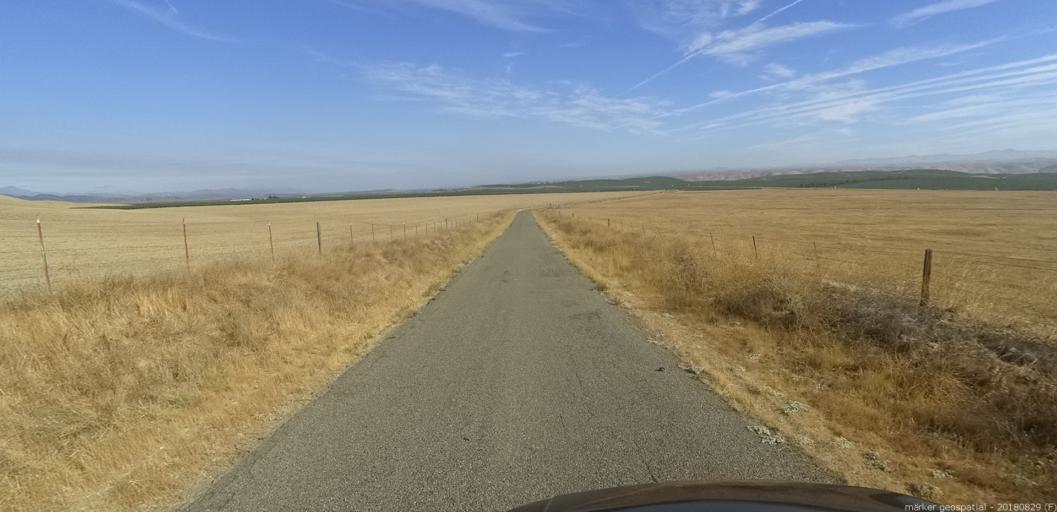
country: US
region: California
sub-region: Monterey County
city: King City
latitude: 36.0504
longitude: -120.9782
